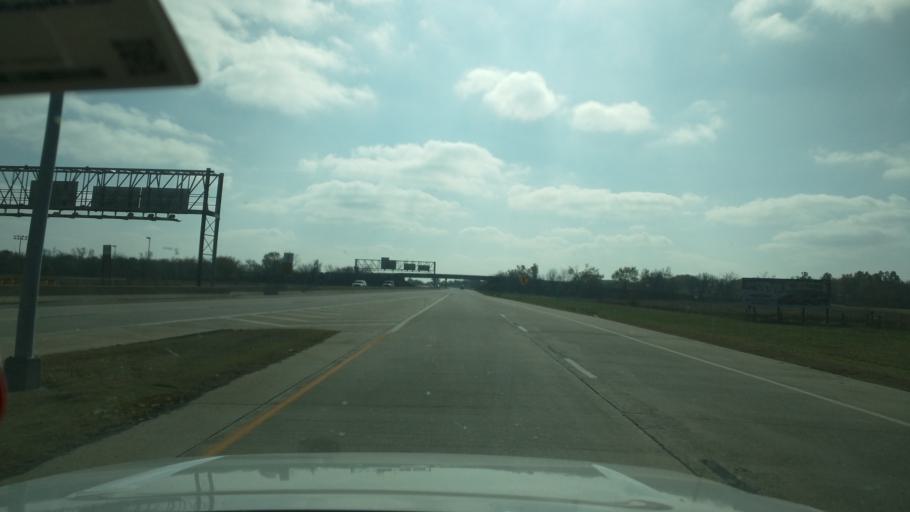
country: US
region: Oklahoma
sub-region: Wagoner County
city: Coweta
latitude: 35.9481
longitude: -95.5893
